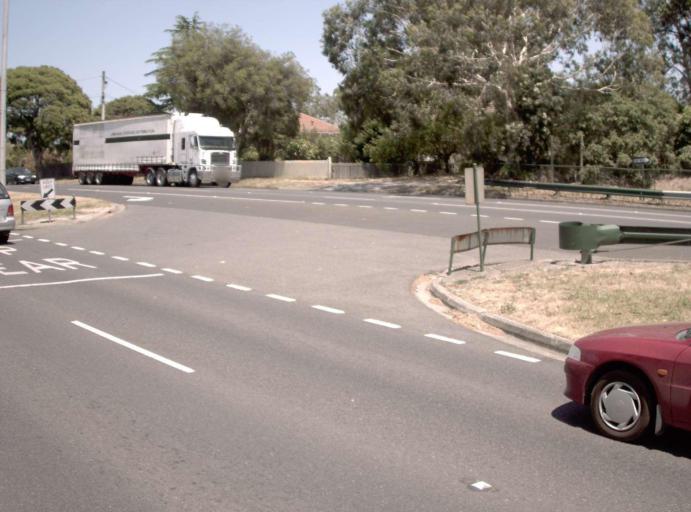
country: AU
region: Victoria
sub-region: Whitehorse
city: Nunawading
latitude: -37.8153
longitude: 145.1767
